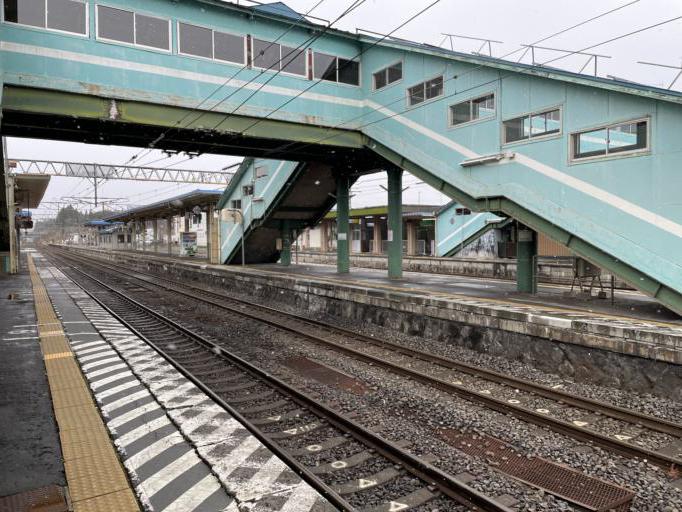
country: JP
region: Aomori
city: Misawa
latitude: 40.8550
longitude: 141.1197
